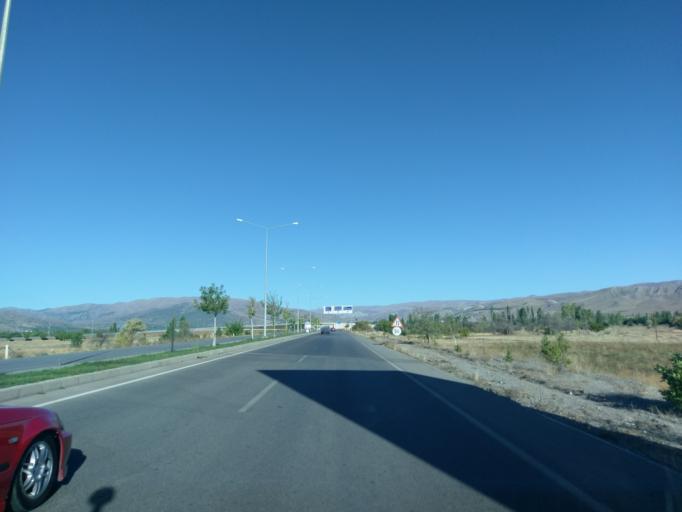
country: TR
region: Erzincan
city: Catalarmut
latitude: 39.7858
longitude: 39.4009
